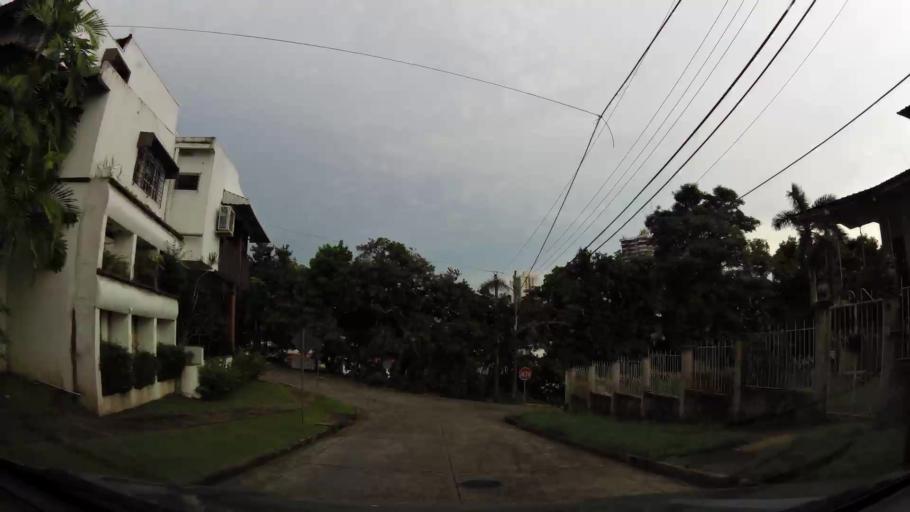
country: PA
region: Panama
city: Panama
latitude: 9.0162
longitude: -79.5237
